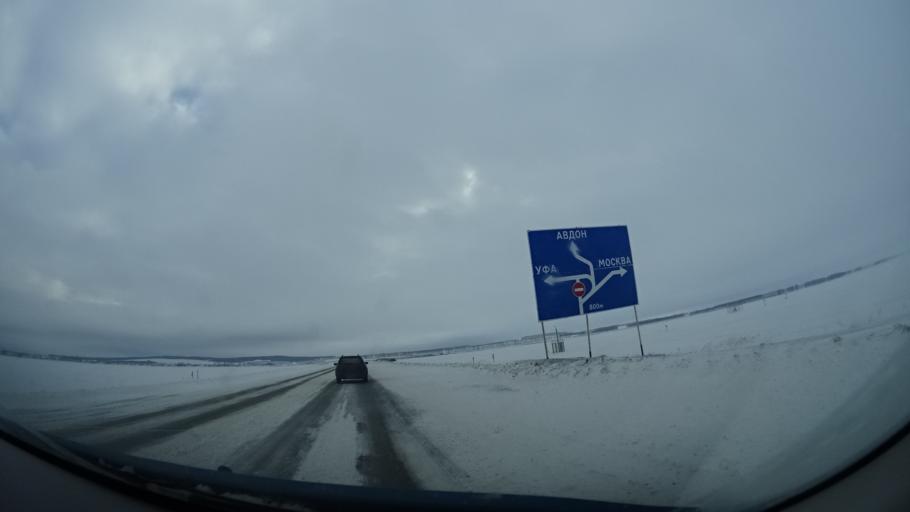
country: RU
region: Bashkortostan
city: Mikhaylovka
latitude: 54.8891
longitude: 55.7192
